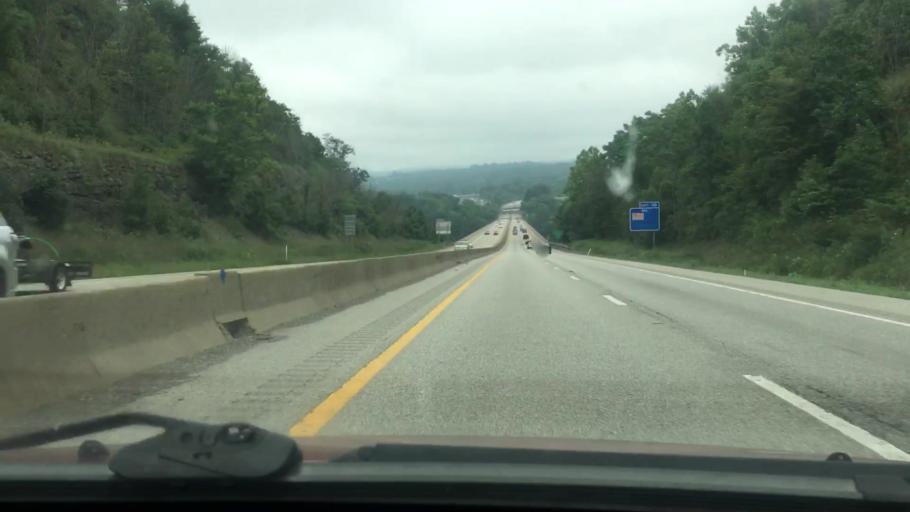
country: US
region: West Virginia
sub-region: Monongalia County
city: Cheat Lake
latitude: 39.6674
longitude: -79.8692
